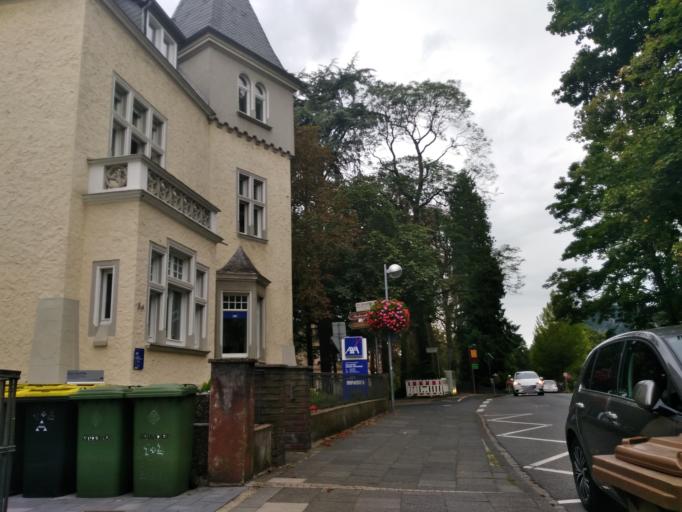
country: DE
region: North Rhine-Westphalia
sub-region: Regierungsbezirk Koln
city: Bad Honnef
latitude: 50.6493
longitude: 7.2209
